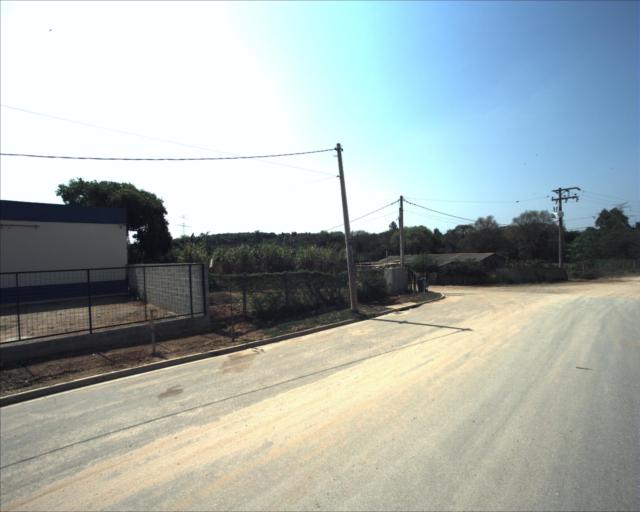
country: BR
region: Sao Paulo
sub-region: Sorocaba
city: Sorocaba
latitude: -23.4189
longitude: -47.4431
